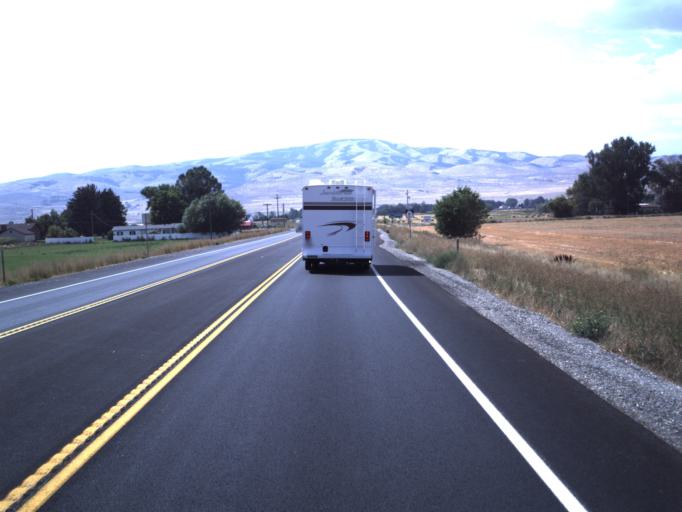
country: US
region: Utah
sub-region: Box Elder County
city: Garland
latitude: 41.7855
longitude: -112.1216
